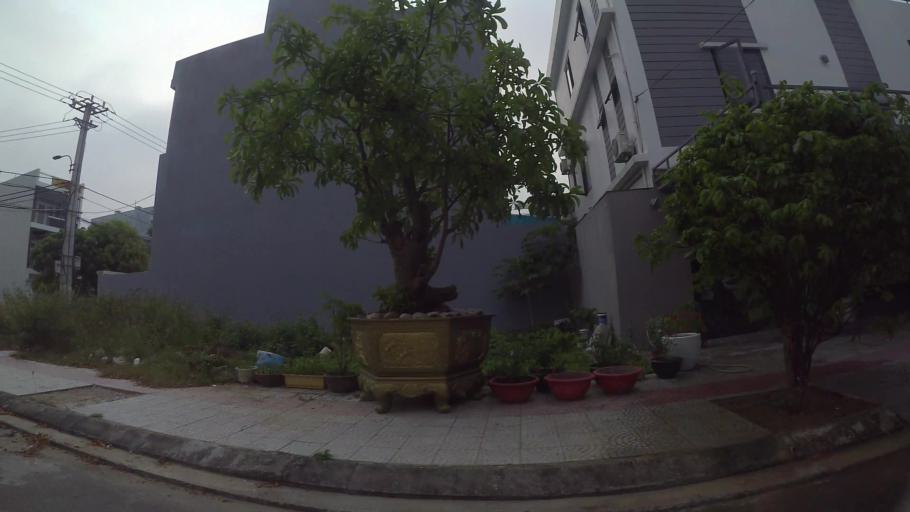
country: VN
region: Da Nang
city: Cam Le
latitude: 16.0221
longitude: 108.2260
